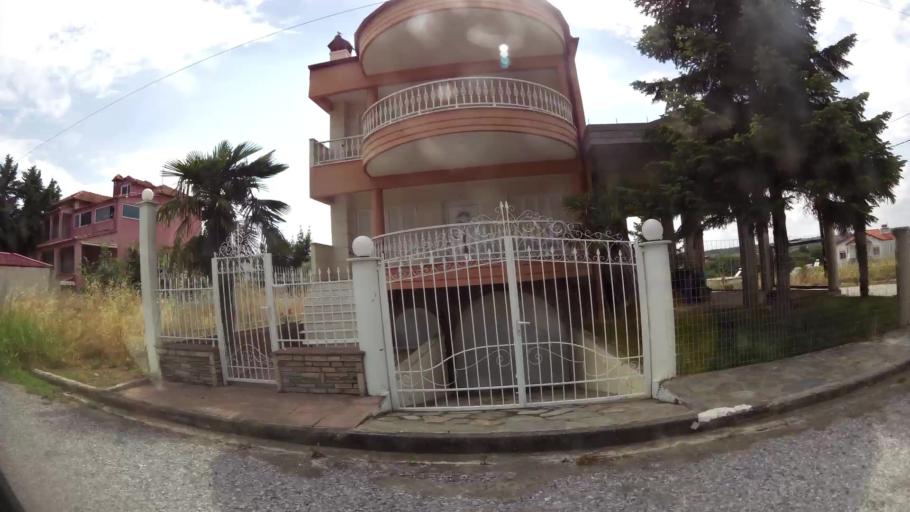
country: GR
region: Central Macedonia
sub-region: Nomos Pierias
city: Makrygialos
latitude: 40.4190
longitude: 22.6073
